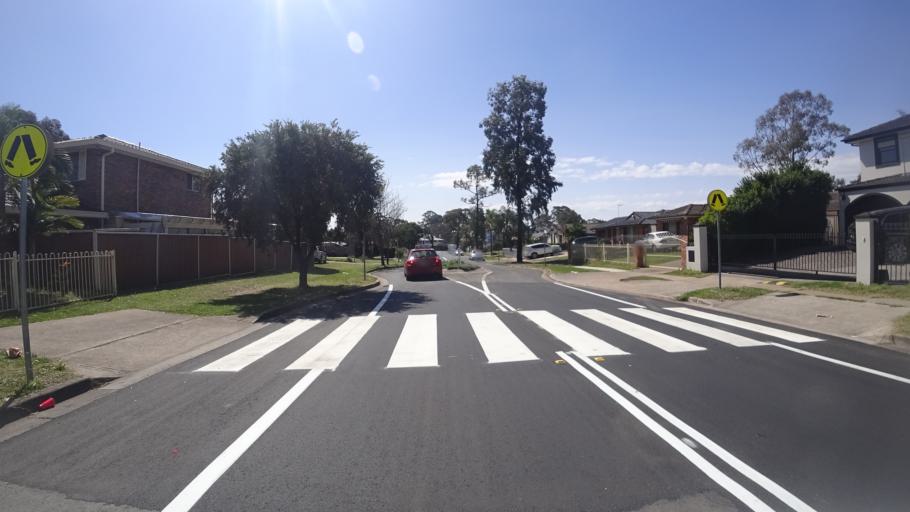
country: AU
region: New South Wales
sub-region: Liverpool
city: Miller
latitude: -33.9420
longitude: 150.8942
